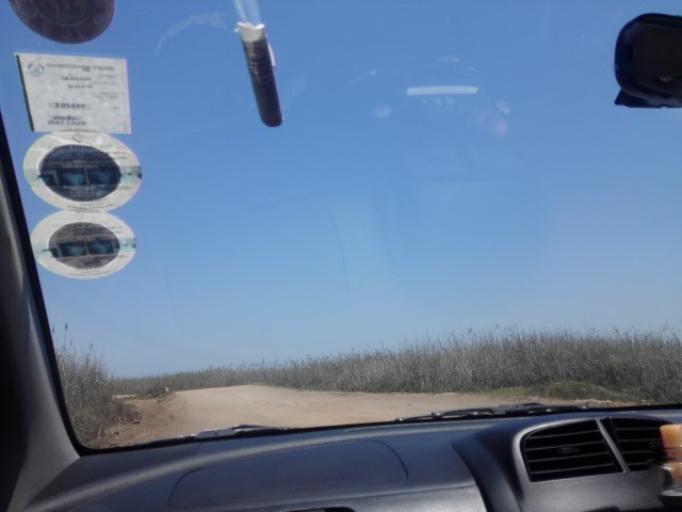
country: MZ
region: Maputo City
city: Maputo
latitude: -25.7318
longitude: 32.7199
